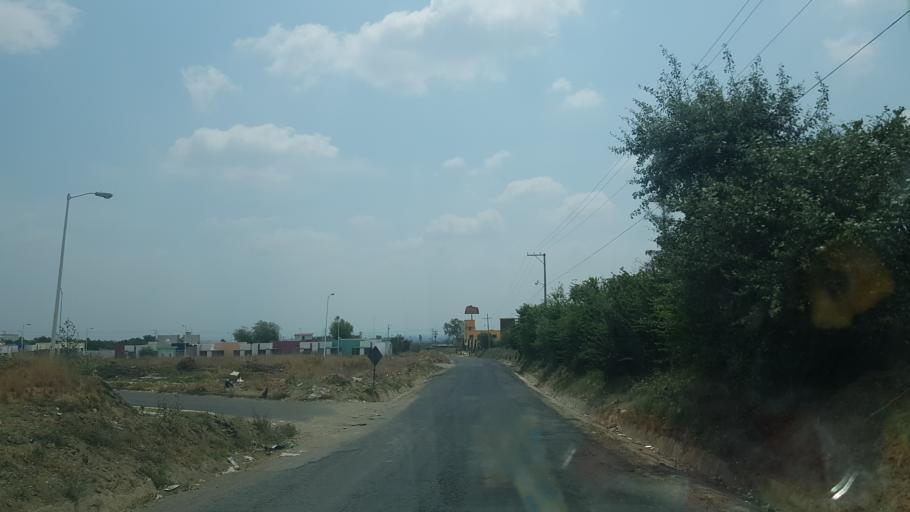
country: MX
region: Puebla
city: Huejotzingo
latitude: 19.1368
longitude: -98.4177
